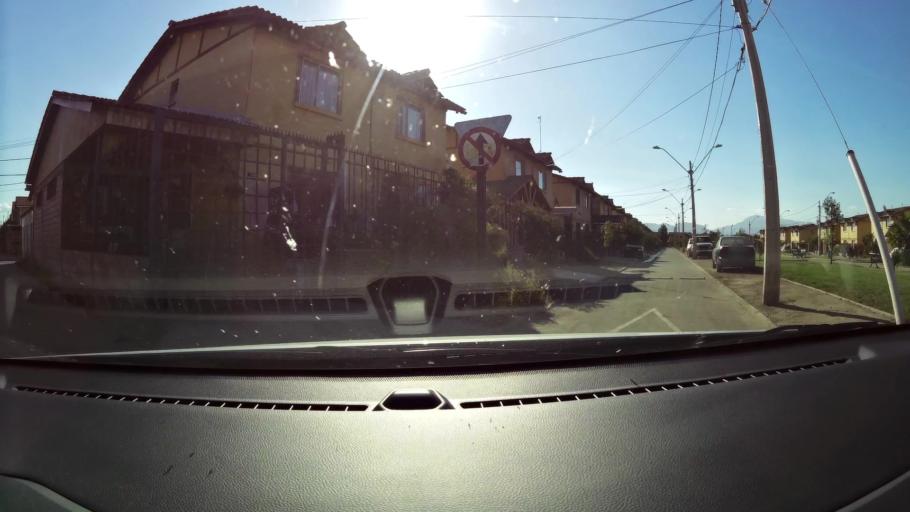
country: CL
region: Santiago Metropolitan
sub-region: Provincia de Maipo
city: San Bernardo
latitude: -33.5488
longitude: -70.7615
